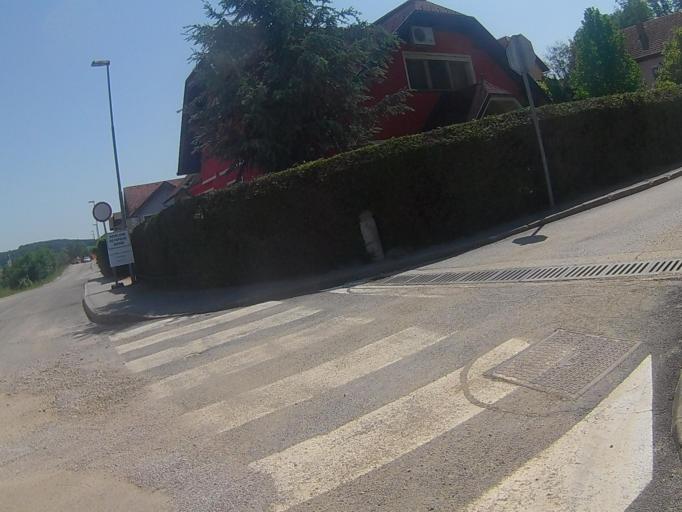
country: SI
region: Pesnica
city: Pesnica pri Mariboru
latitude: 46.5783
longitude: 15.7170
